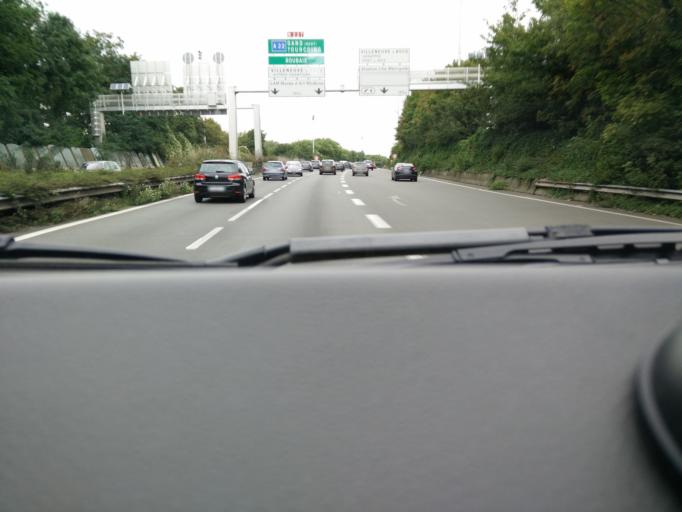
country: FR
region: Nord-Pas-de-Calais
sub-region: Departement du Nord
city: Mons-en-Baroeul
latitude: 50.6220
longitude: 3.1346
